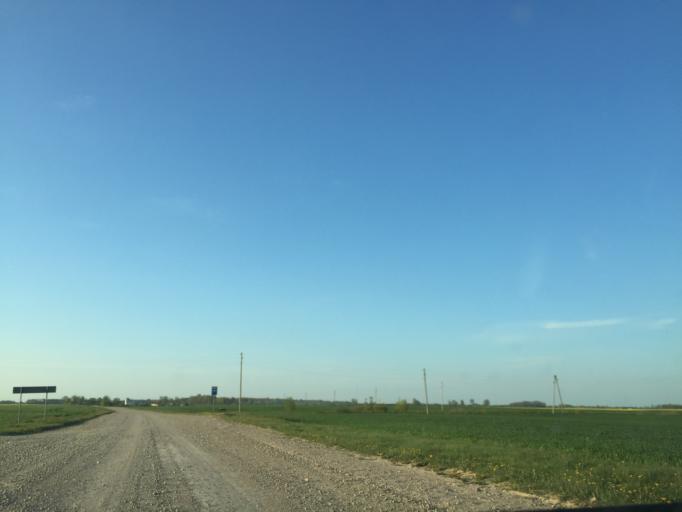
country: LV
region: Bauskas Rajons
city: Bauska
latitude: 56.2886
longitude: 24.1979
